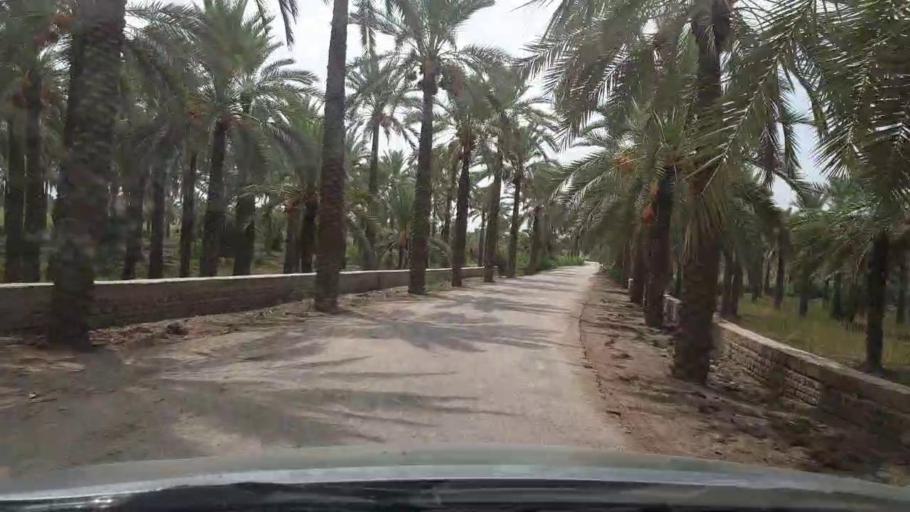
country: PK
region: Sindh
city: Kot Diji
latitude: 27.4047
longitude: 68.7416
